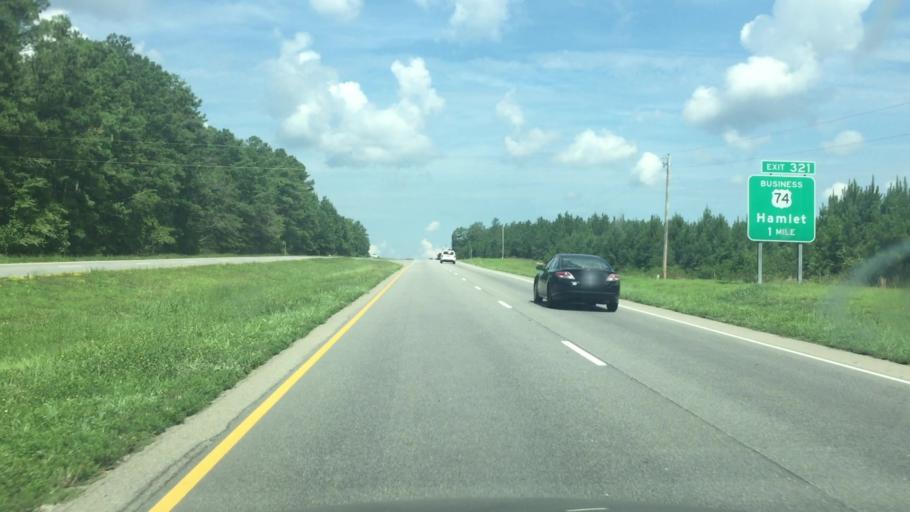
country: US
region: North Carolina
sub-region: Richmond County
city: Hamlet
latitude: 34.8598
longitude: -79.6307
